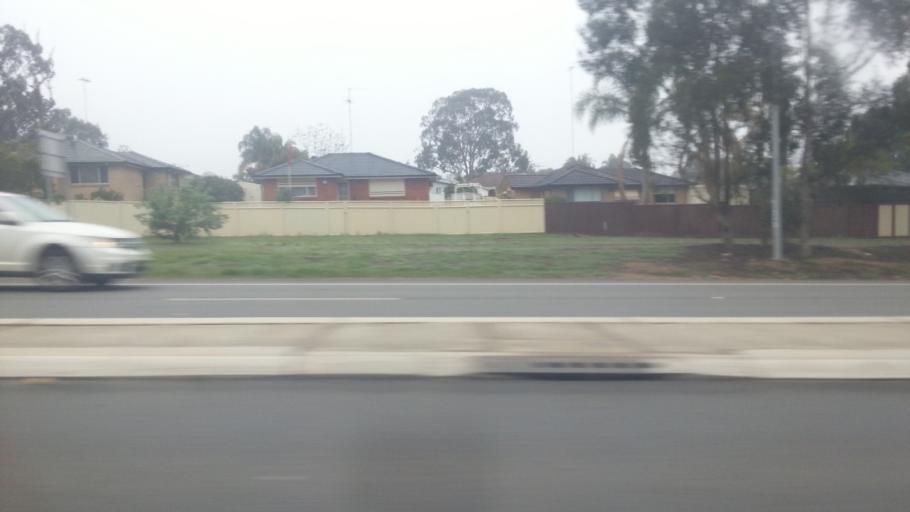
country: AU
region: New South Wales
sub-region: Penrith Municipality
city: Werrington Downs
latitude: -33.7330
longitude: 150.7179
